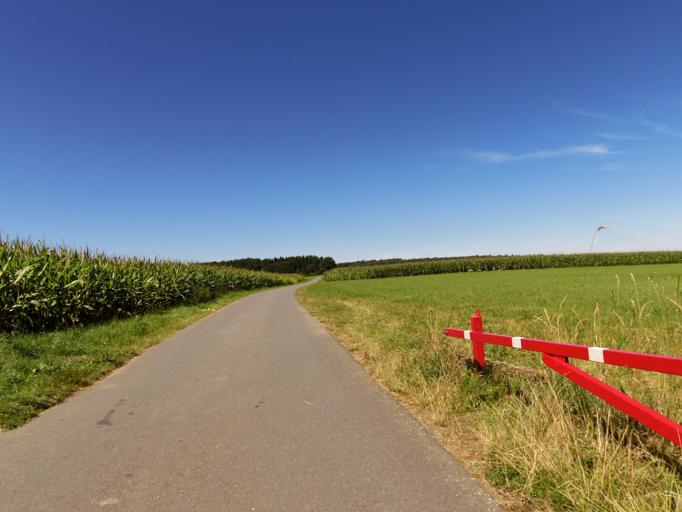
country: DE
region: Hesse
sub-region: Regierungsbezirk Darmstadt
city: Erbach
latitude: 49.6757
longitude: 8.9402
